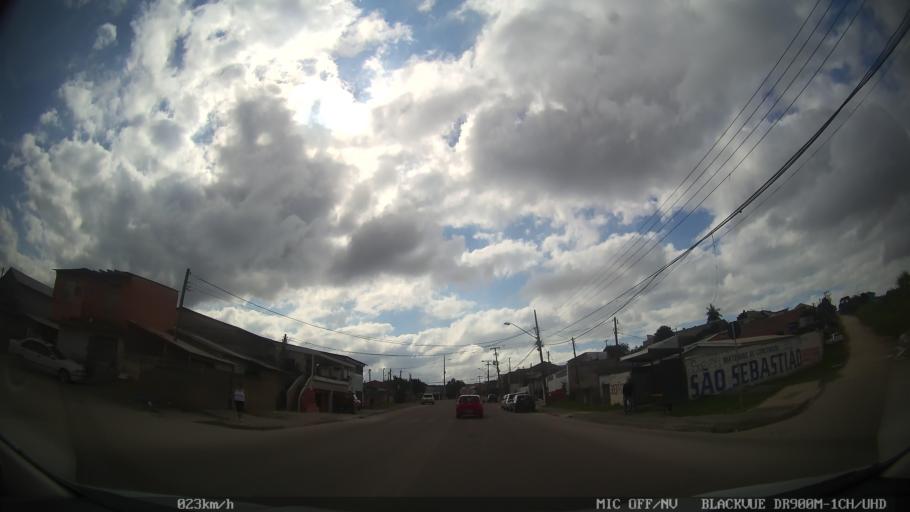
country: BR
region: Parana
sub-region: Colombo
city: Colombo
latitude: -25.3629
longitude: -49.1961
